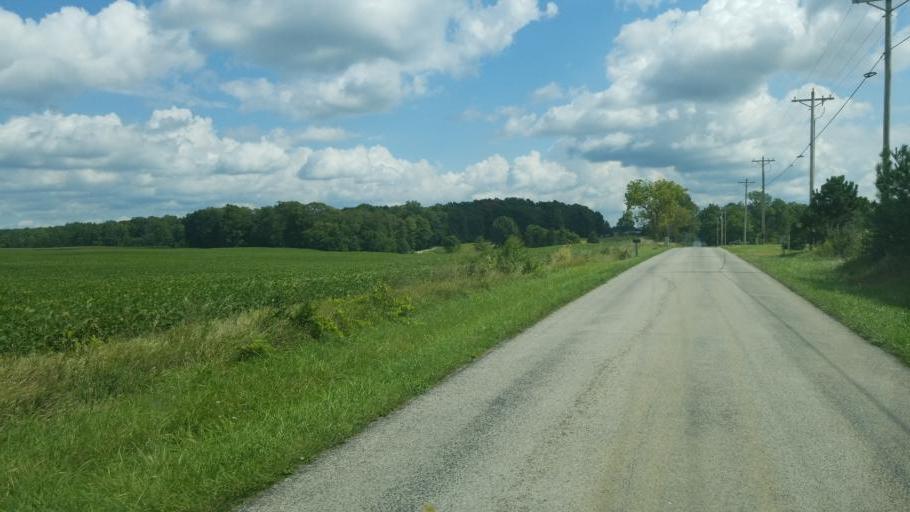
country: US
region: Ohio
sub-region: Huron County
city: Monroeville
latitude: 41.1648
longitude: -82.6809
